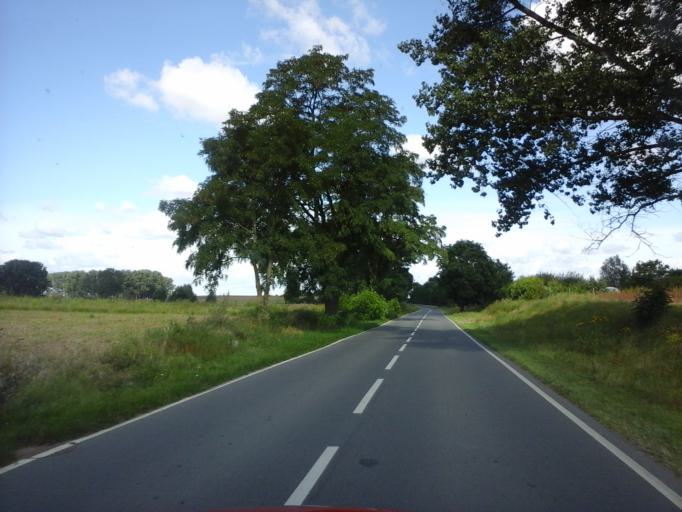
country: PL
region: West Pomeranian Voivodeship
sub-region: Powiat stargardzki
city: Dolice
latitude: 53.1936
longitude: 15.1920
